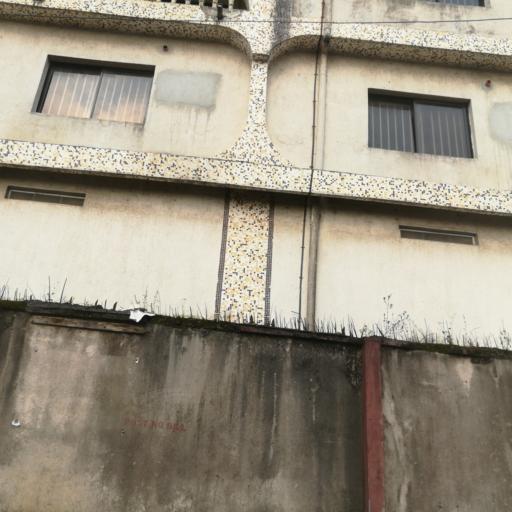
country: NG
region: Rivers
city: Port Harcourt
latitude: 4.8492
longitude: 7.0543
